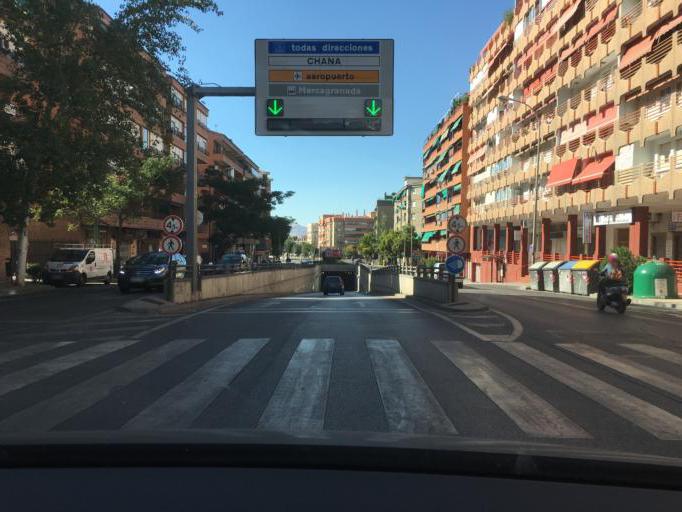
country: ES
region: Andalusia
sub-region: Provincia de Granada
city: Granada
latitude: 37.1883
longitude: -3.6127
